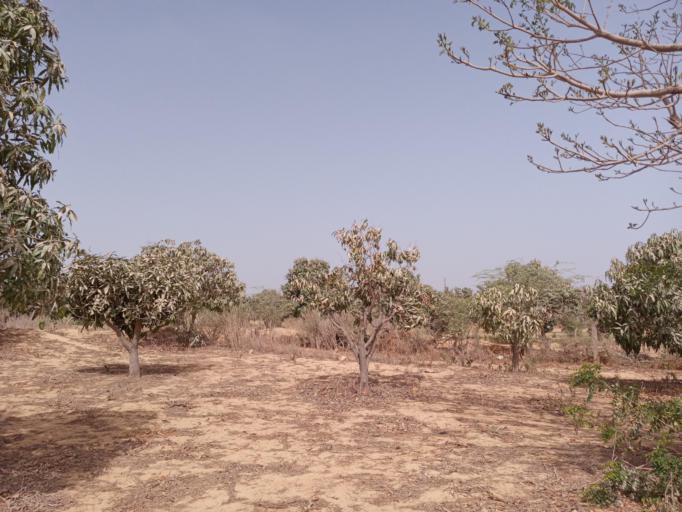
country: SN
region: Thies
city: Mekhe
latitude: 15.1086
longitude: -16.8396
